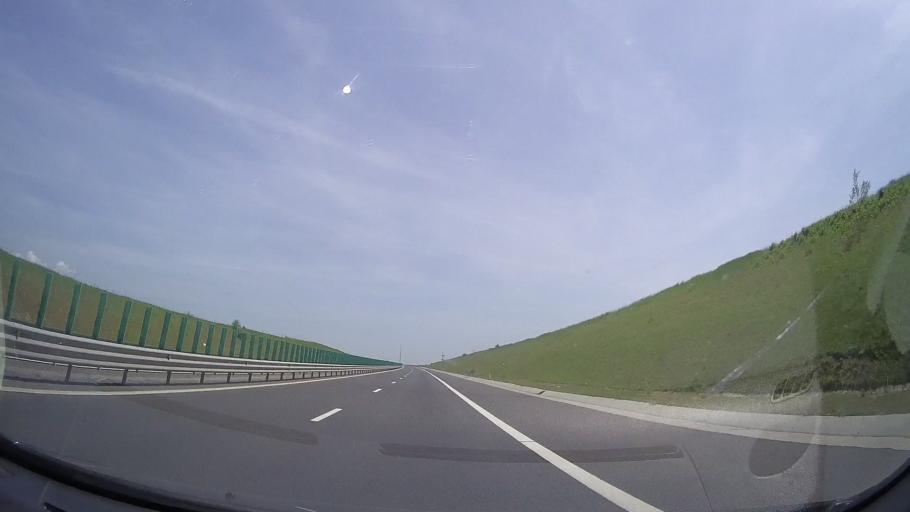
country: RO
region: Hunedoara
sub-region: Comuna Romos
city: Romos
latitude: 45.8966
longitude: 23.2892
